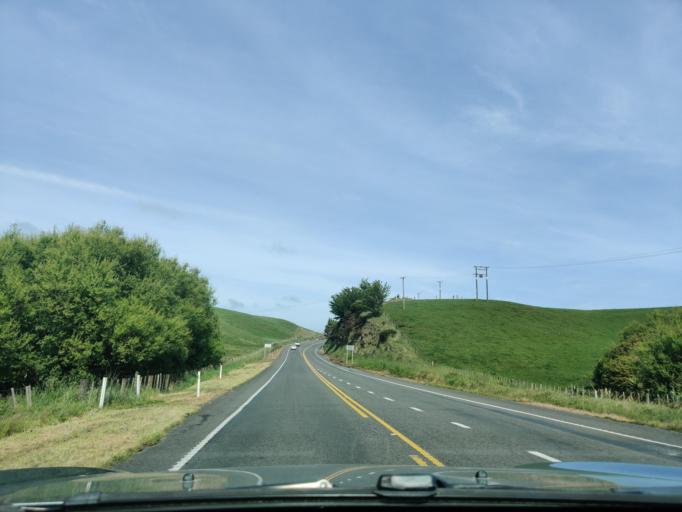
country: NZ
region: Taranaki
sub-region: South Taranaki District
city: Patea
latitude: -39.6857
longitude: 174.4192
